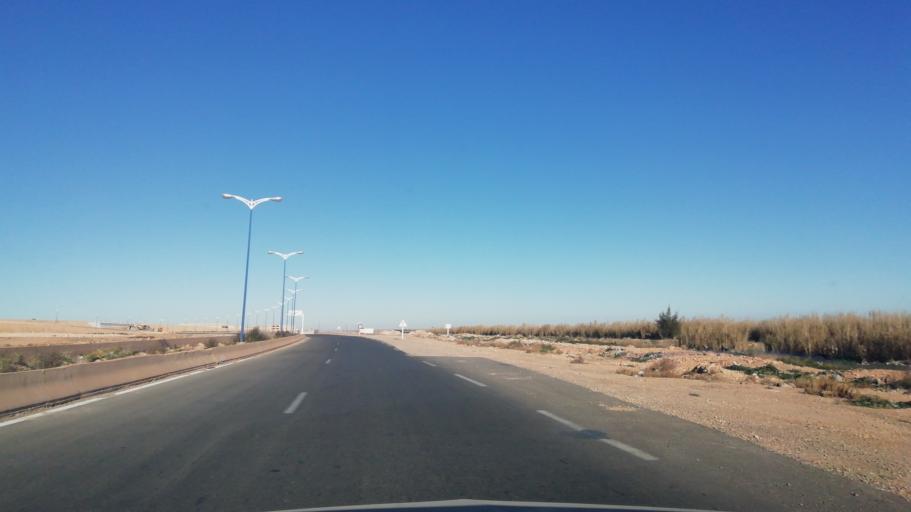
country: DZ
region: Wilaya de Naama
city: Naama
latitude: 33.5518
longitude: -0.2402
